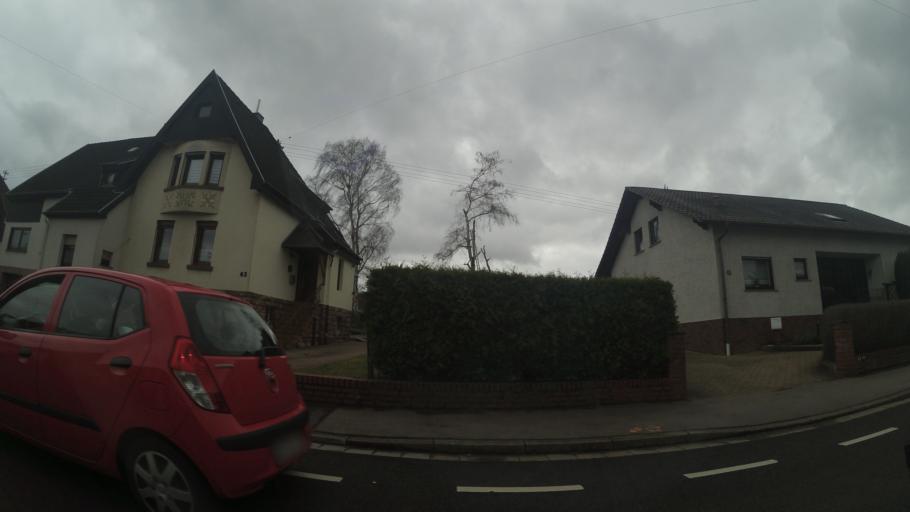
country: DE
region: Saarland
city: Schwalbach
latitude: 49.3028
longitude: 6.8071
